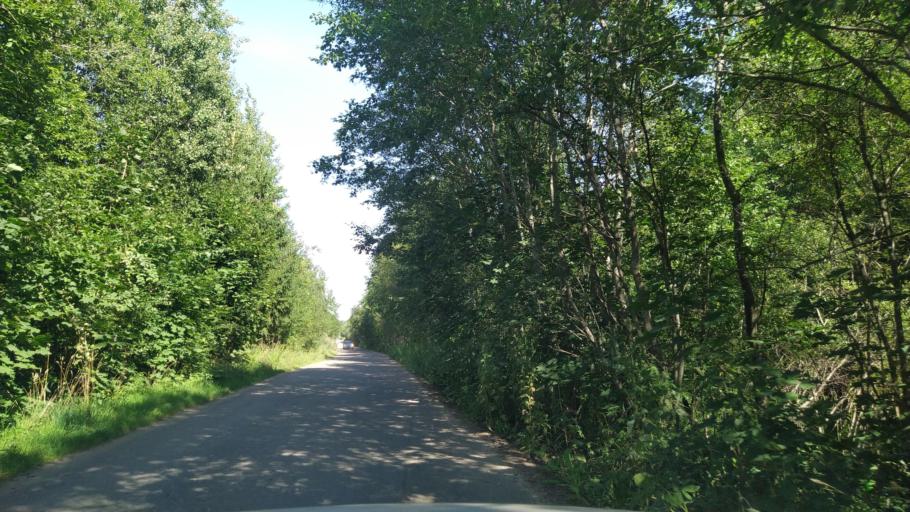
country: RU
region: Leningrad
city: Siverskiy
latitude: 59.2807
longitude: 30.0288
